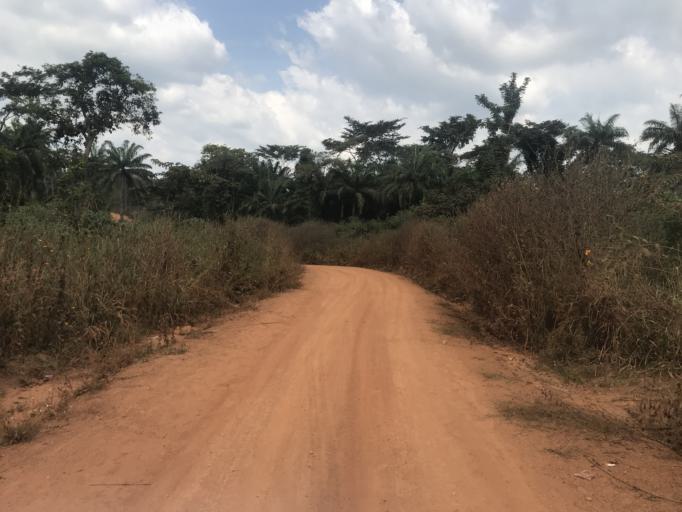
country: NG
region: Osun
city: Inisa
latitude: 7.8638
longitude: 4.3841
